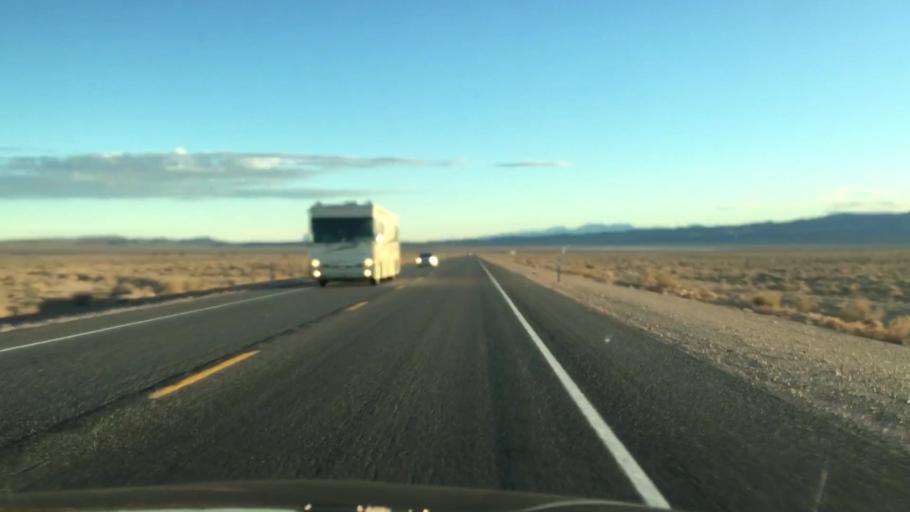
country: US
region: Nevada
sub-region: Esmeralda County
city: Goldfield
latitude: 37.5218
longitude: -117.1900
